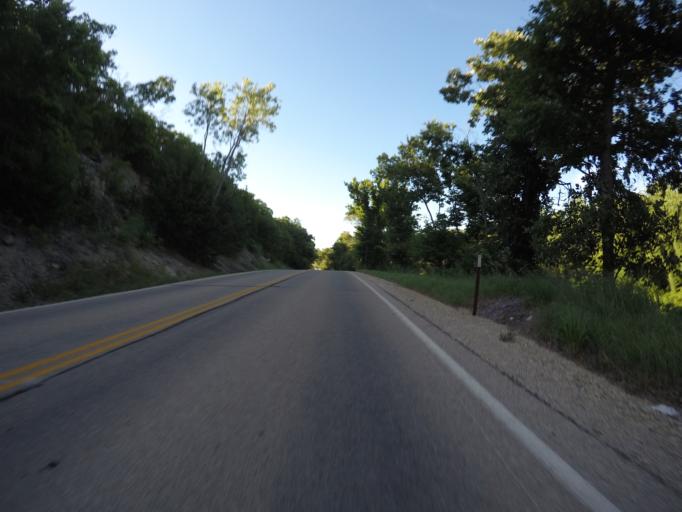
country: US
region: Kansas
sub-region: Riley County
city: Manhattan
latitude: 39.1621
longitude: -96.5955
